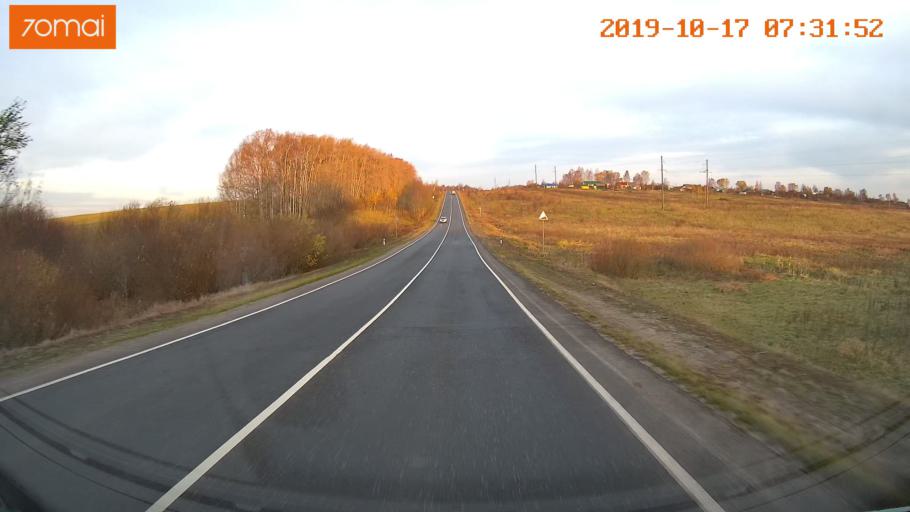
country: RU
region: Ivanovo
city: Gavrilov Posad
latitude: 56.3934
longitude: 39.9871
